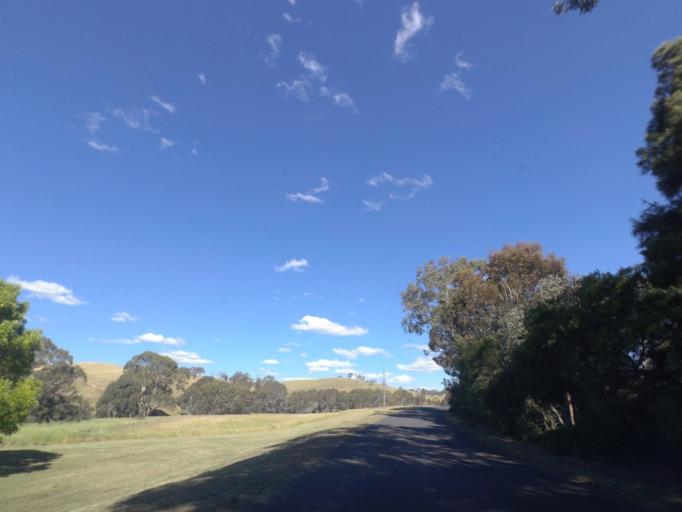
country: AU
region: Victoria
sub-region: Hume
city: Craigieburn
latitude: -37.4046
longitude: 144.9007
